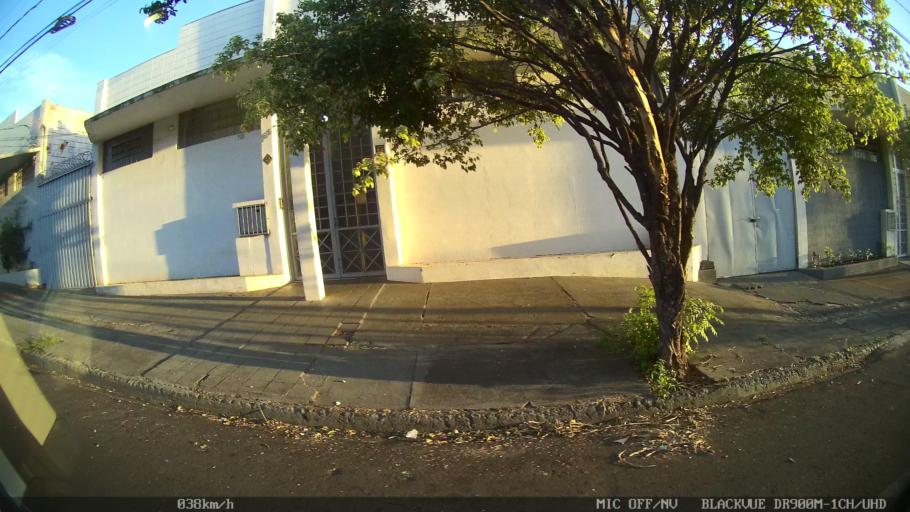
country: BR
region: Sao Paulo
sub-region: Franca
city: Franca
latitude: -20.5168
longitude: -47.4133
